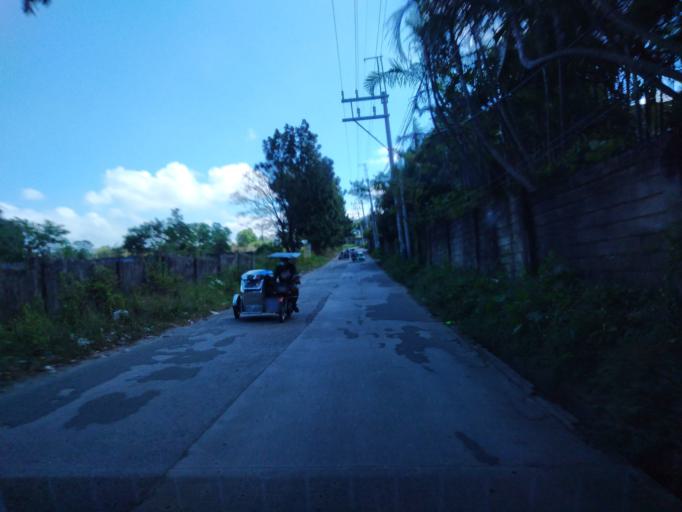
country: PH
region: Central Luzon
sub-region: Province of Bulacan
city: Bitungol
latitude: 14.8580
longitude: 121.0440
